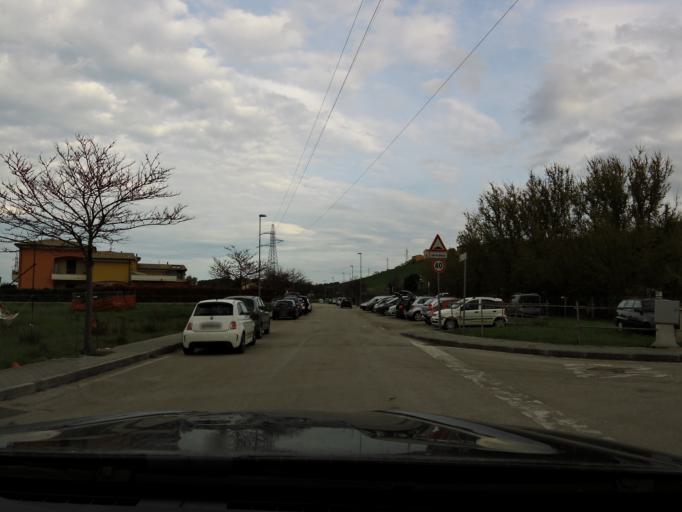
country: IT
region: The Marches
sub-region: Provincia di Ancona
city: Loreto Stazione
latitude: 43.4454
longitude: 13.6220
